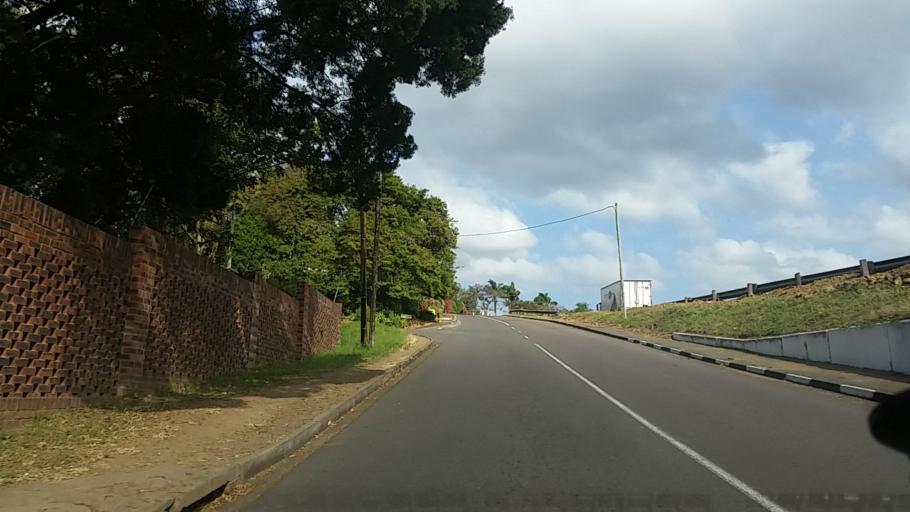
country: ZA
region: KwaZulu-Natal
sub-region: eThekwini Metropolitan Municipality
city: Berea
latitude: -29.8298
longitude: 30.9566
